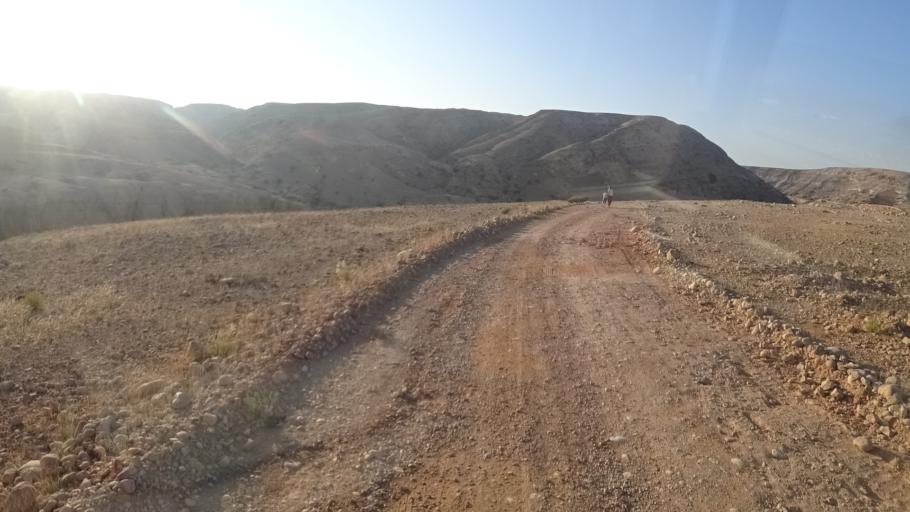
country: OM
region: Zufar
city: Salalah
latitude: 17.2439
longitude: 53.8910
